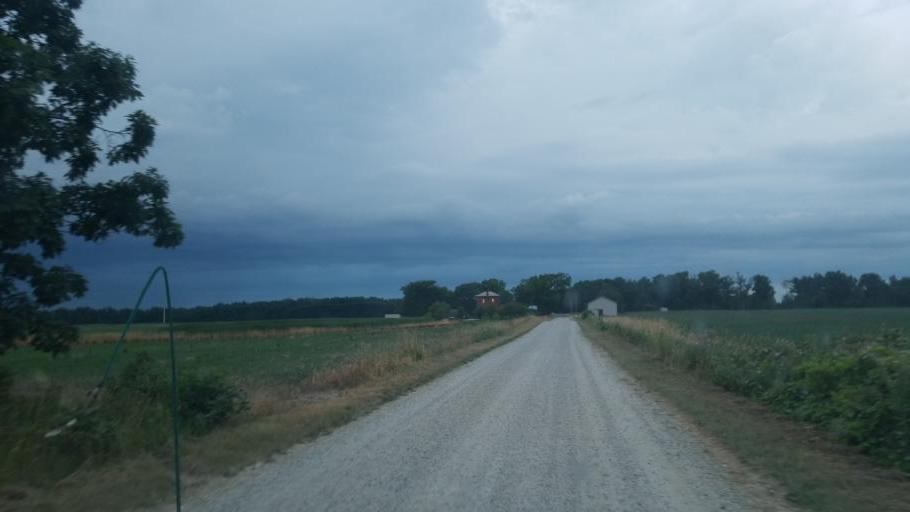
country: US
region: Ohio
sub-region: Defiance County
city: Hicksville
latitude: 41.3290
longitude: -84.8104
